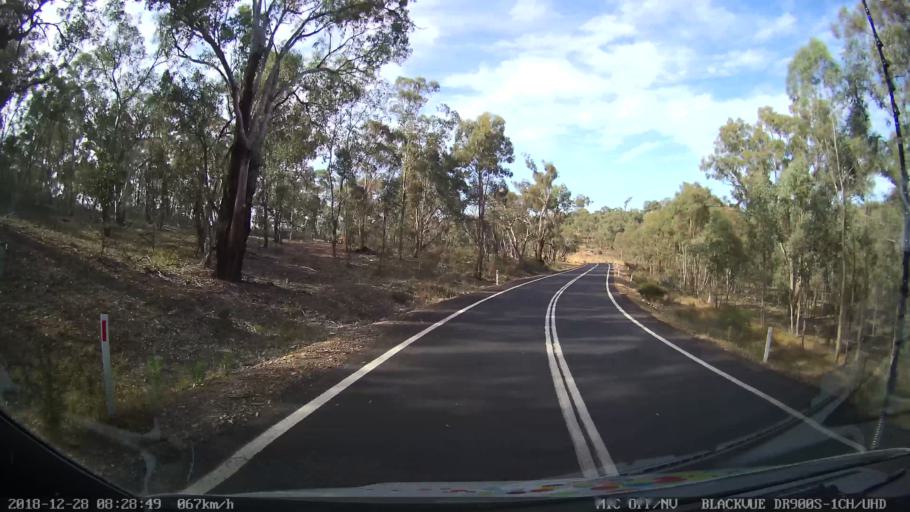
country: AU
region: New South Wales
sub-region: Blayney
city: Blayney
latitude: -33.9439
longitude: 149.3249
